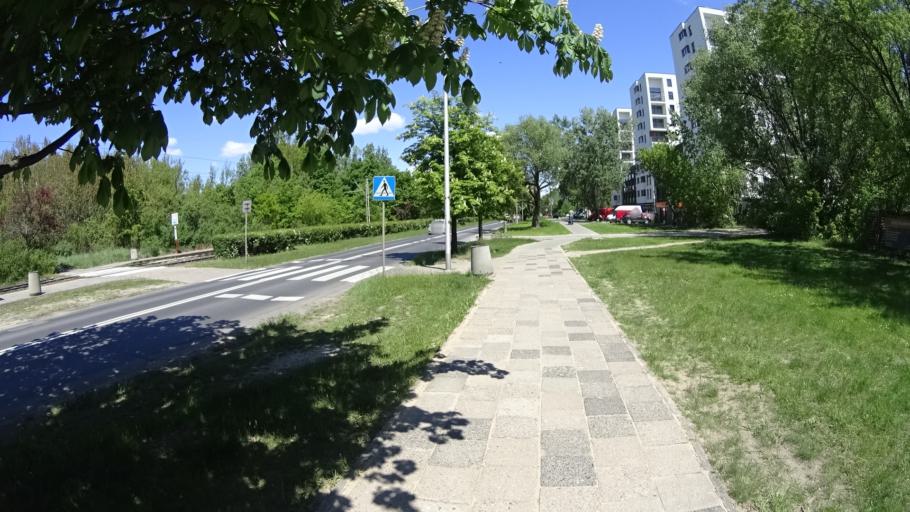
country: PL
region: Masovian Voivodeship
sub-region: Warszawa
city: Bielany
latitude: 52.2845
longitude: 20.9229
